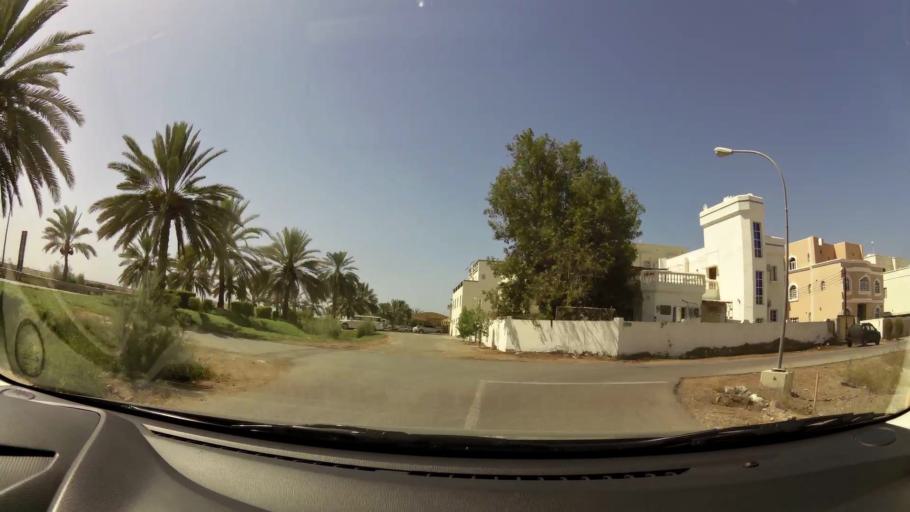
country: OM
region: Muhafazat Masqat
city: Bawshar
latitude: 23.5975
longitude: 58.3476
